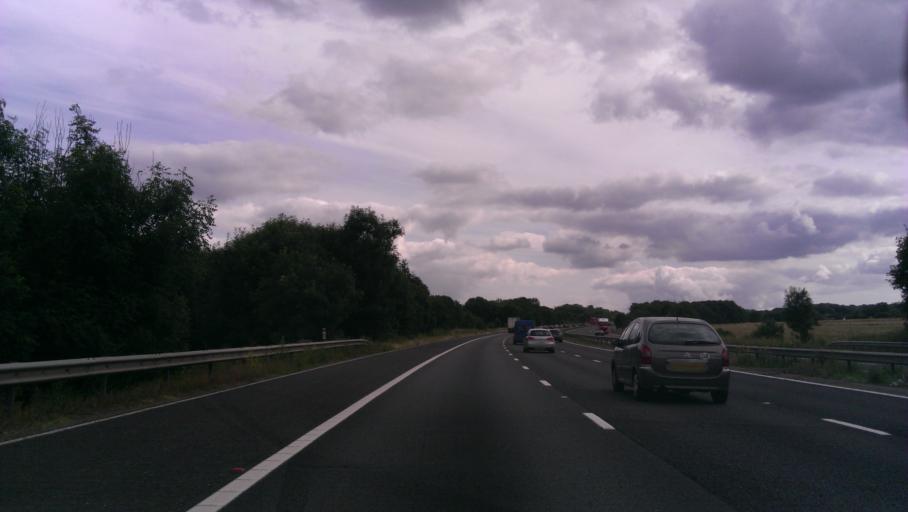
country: GB
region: England
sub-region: Kent
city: Longfield
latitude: 51.3453
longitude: 0.2762
